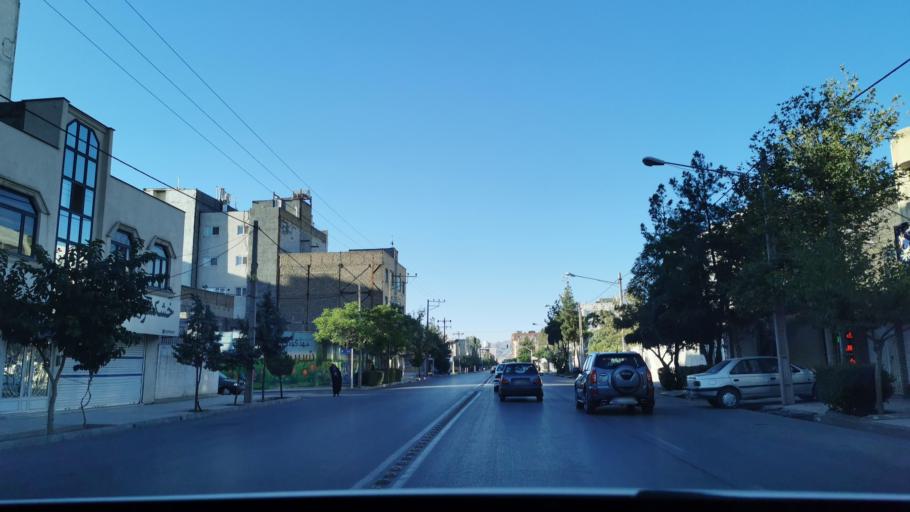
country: IR
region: Razavi Khorasan
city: Mashhad
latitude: 36.3535
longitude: 59.4973
